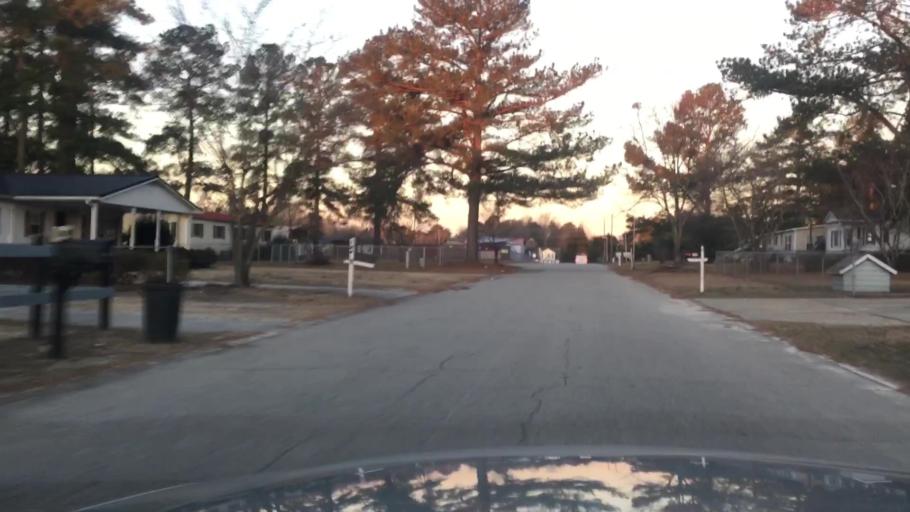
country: US
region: North Carolina
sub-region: Cumberland County
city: Hope Mills
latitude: 34.9906
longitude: -78.9010
